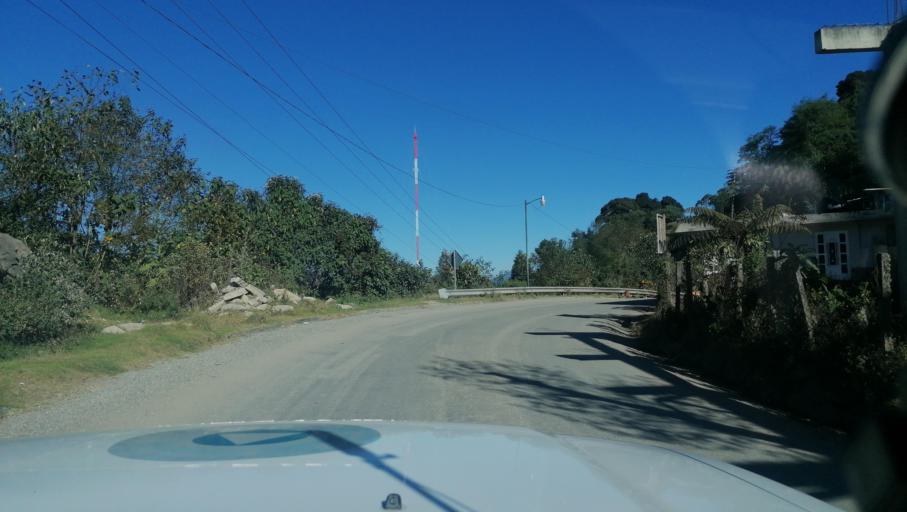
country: MX
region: Chiapas
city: Motozintla de Mendoza
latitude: 15.2611
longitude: -92.2148
